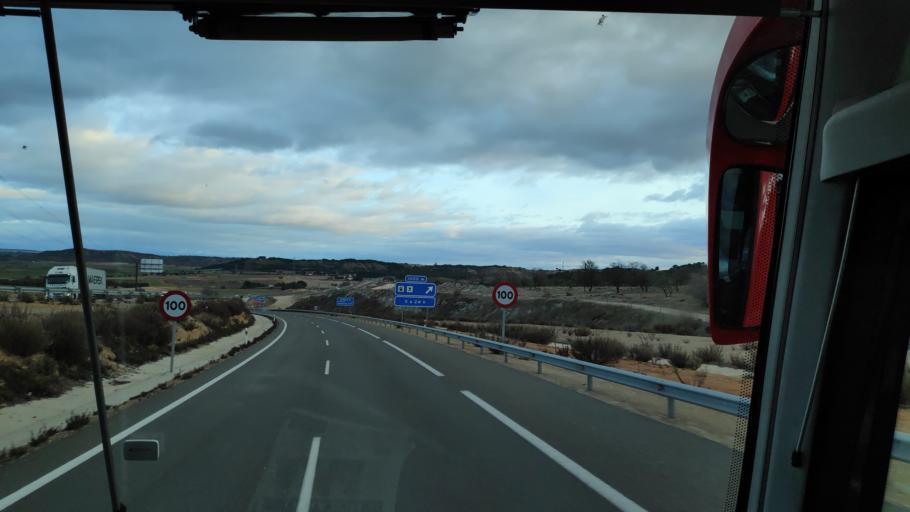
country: ES
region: Castille-La Mancha
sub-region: Provincia de Cuenca
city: Belinchon
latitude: 40.0443
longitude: -3.0606
